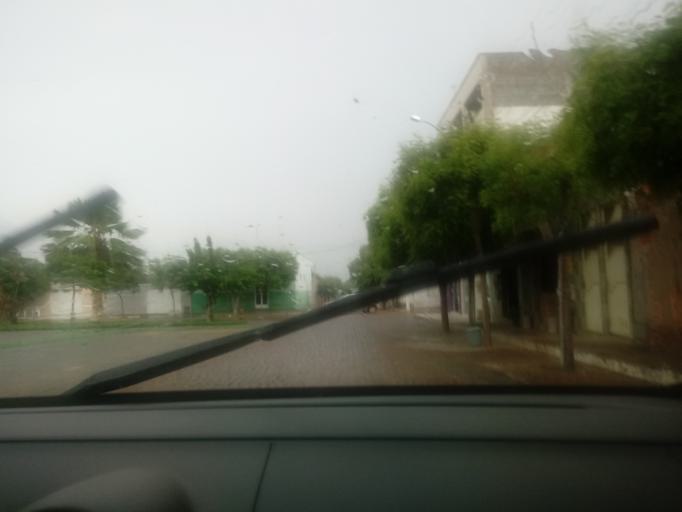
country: BR
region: Bahia
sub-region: Riacho De Santana
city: Riacho de Santana
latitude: -13.9100
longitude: -42.8458
